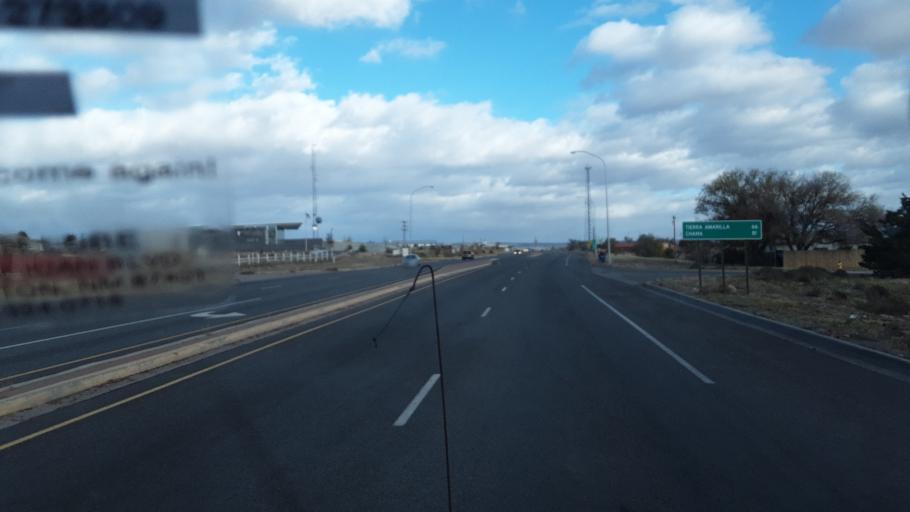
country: US
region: New Mexico
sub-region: Rio Arriba County
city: Espanola
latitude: 36.0088
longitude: -106.0879
